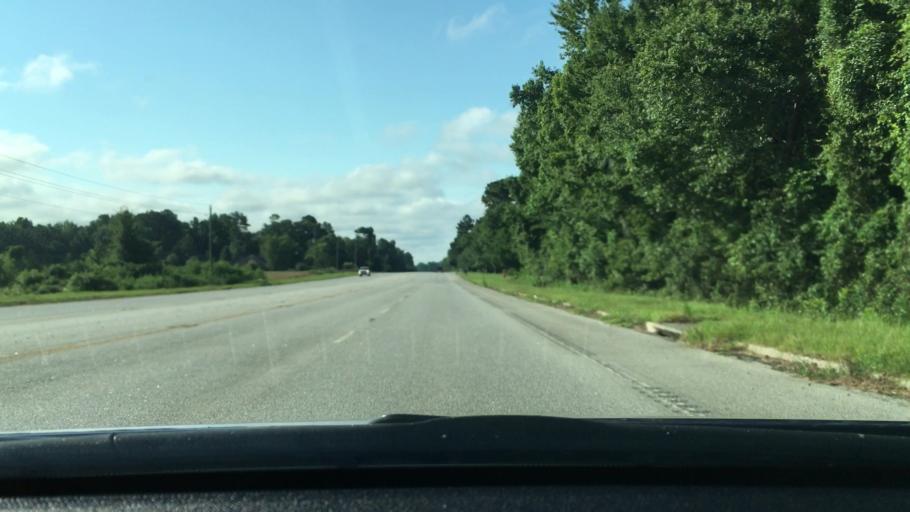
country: US
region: South Carolina
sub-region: Clarendon County
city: Manning
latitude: 33.7608
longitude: -80.2288
